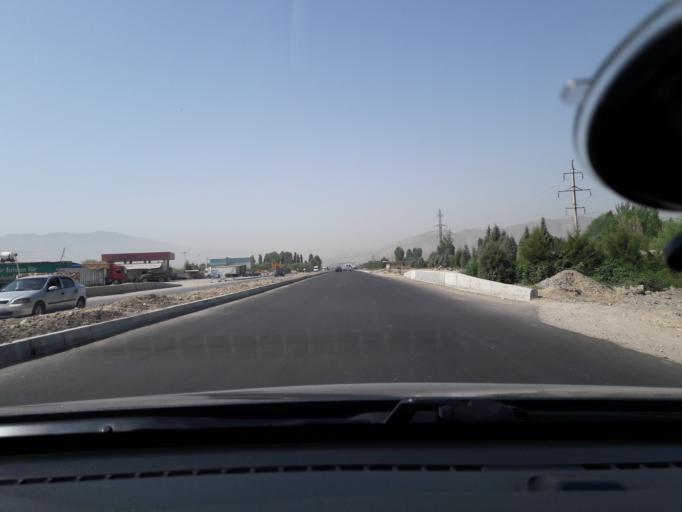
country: TJ
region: Dushanbe
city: Dushanbe
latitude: 38.4846
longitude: 68.7485
